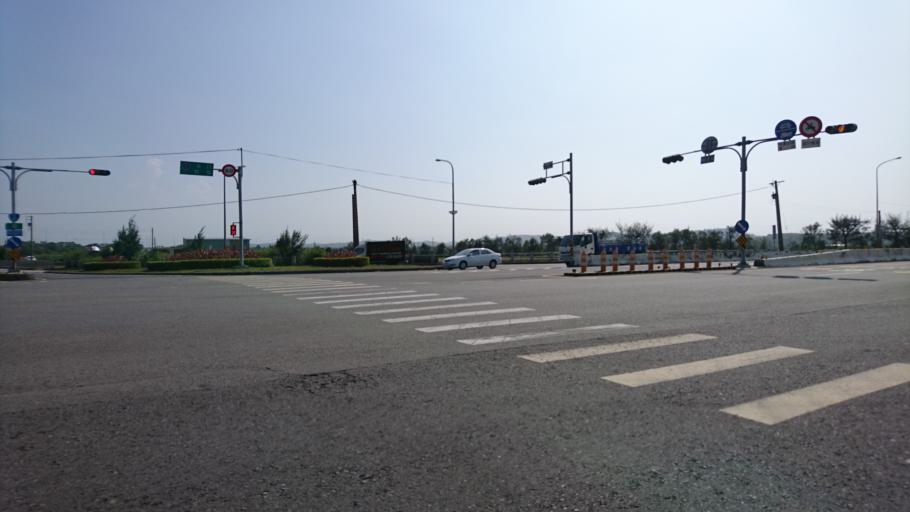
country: TW
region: Taiwan
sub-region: Miaoli
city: Miaoli
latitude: 24.6777
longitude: 120.8435
